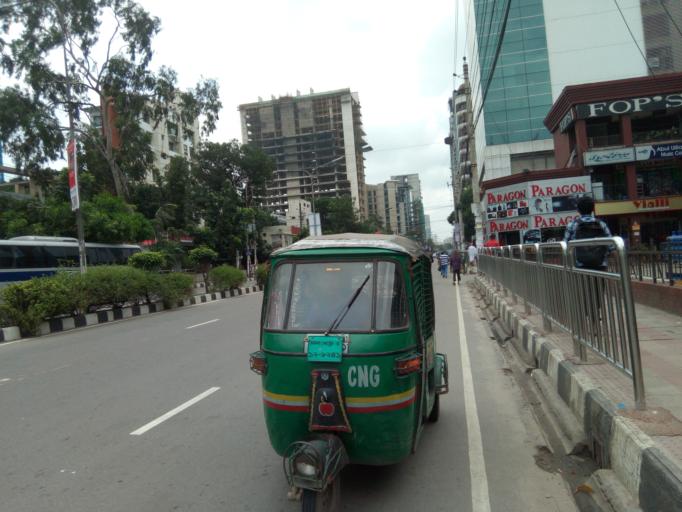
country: BD
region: Dhaka
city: Paltan
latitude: 23.7942
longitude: 90.4020
